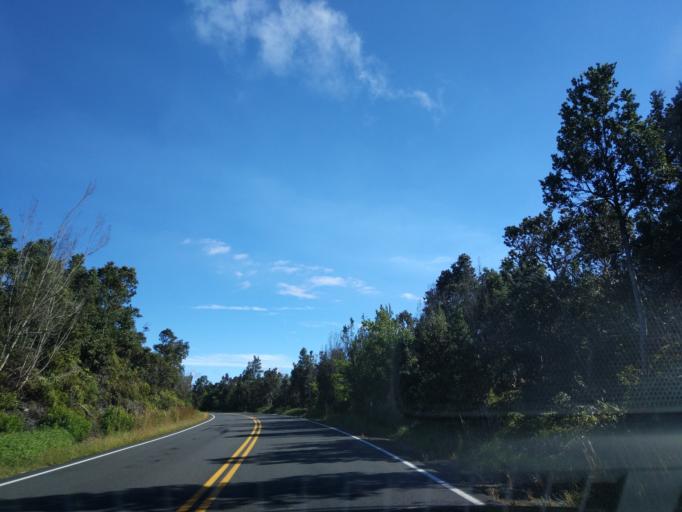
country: US
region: Hawaii
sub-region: Hawaii County
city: Volcano
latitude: 19.3688
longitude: -155.2250
